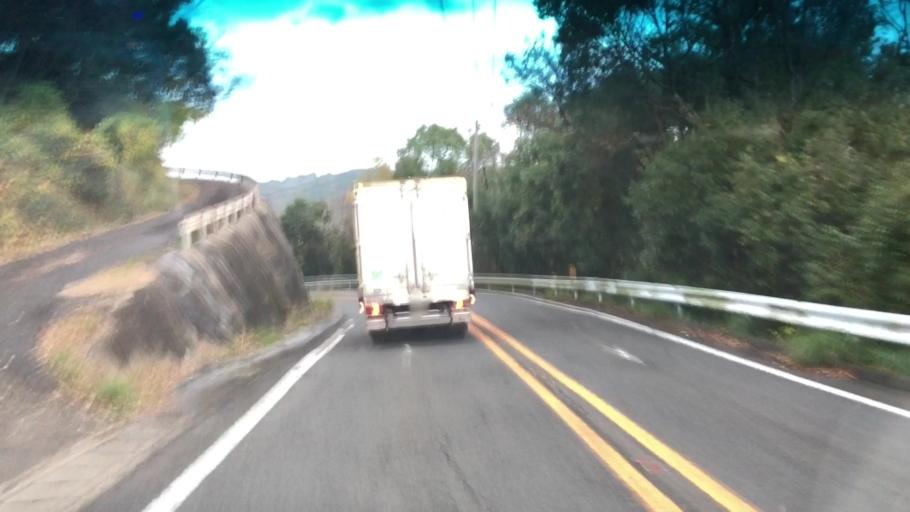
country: JP
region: Nagasaki
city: Sasebo
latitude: 33.0471
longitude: 129.7169
